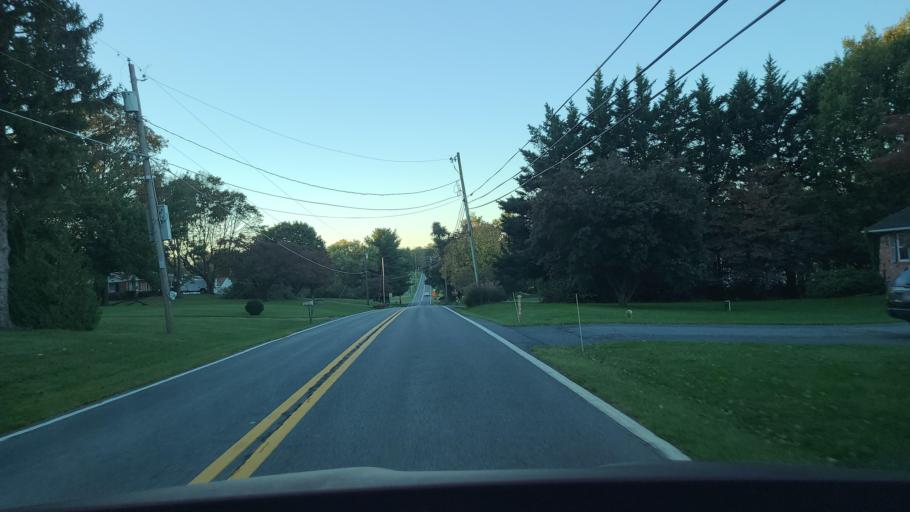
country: US
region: Maryland
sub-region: Frederick County
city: Jefferson
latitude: 39.3672
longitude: -77.5387
